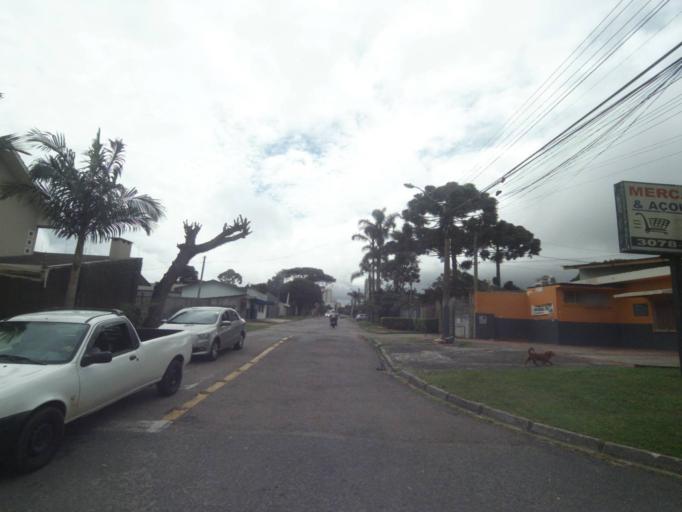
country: BR
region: Parana
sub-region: Curitiba
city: Curitiba
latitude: -25.4863
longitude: -49.2996
